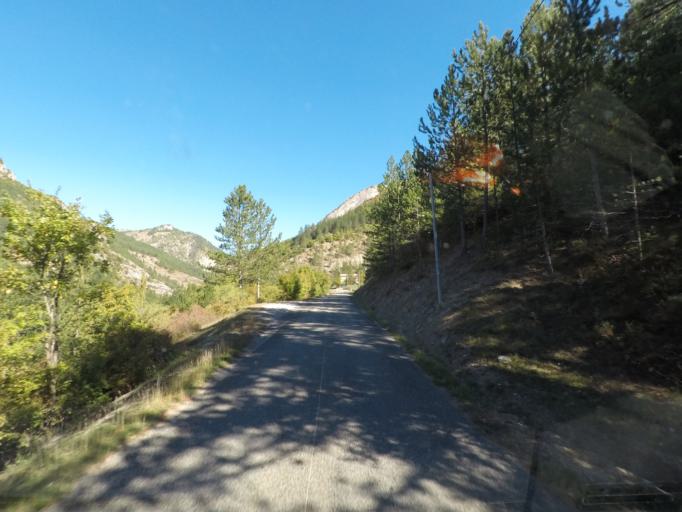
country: FR
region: Rhone-Alpes
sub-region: Departement de la Drome
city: Die
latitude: 44.5960
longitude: 5.2839
